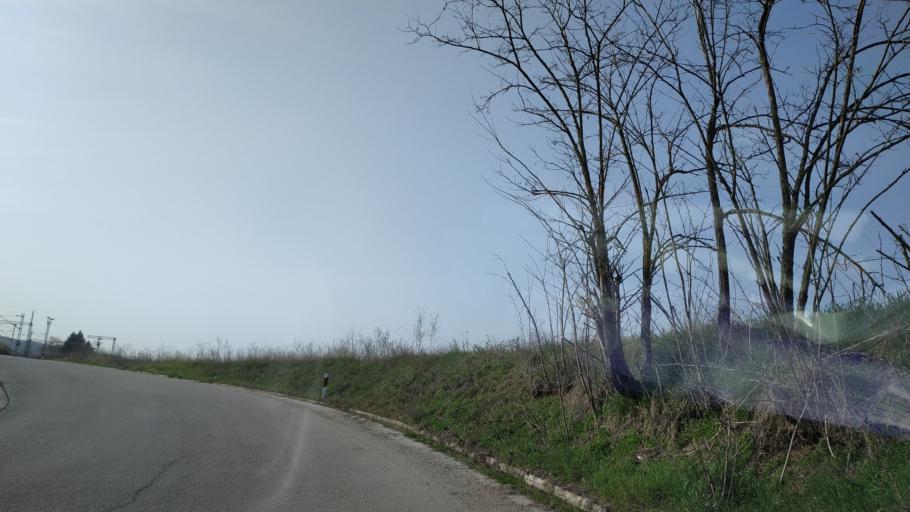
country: RS
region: Central Serbia
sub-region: Nisavski Okrug
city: Aleksinac
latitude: 43.5205
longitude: 21.6571
